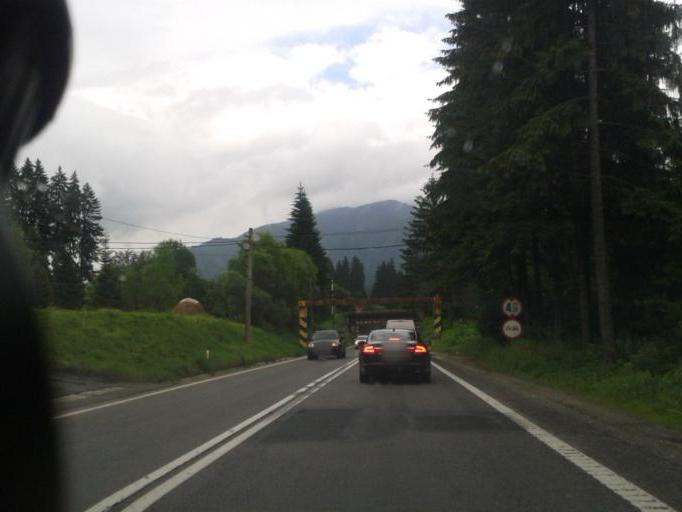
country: RO
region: Brasov
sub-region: Oras Predeal
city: Predeal
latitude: 45.5248
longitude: 25.5733
